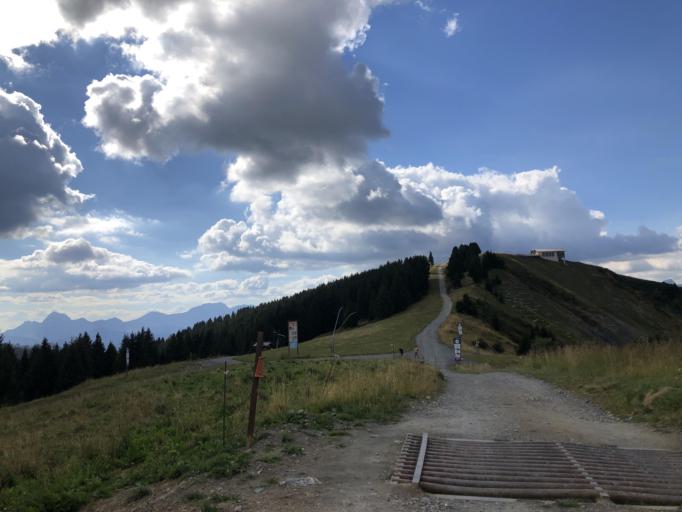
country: FR
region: Rhone-Alpes
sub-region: Departement de la Haute-Savoie
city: Les Contamines-Montjoie
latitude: 45.8441
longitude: 6.6821
